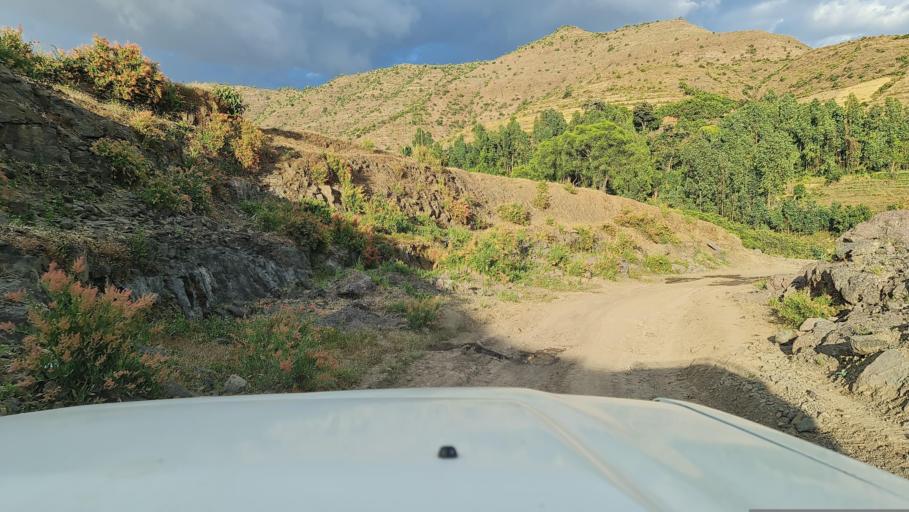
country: ET
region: Amhara
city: Debark'
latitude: 13.0413
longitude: 38.0369
